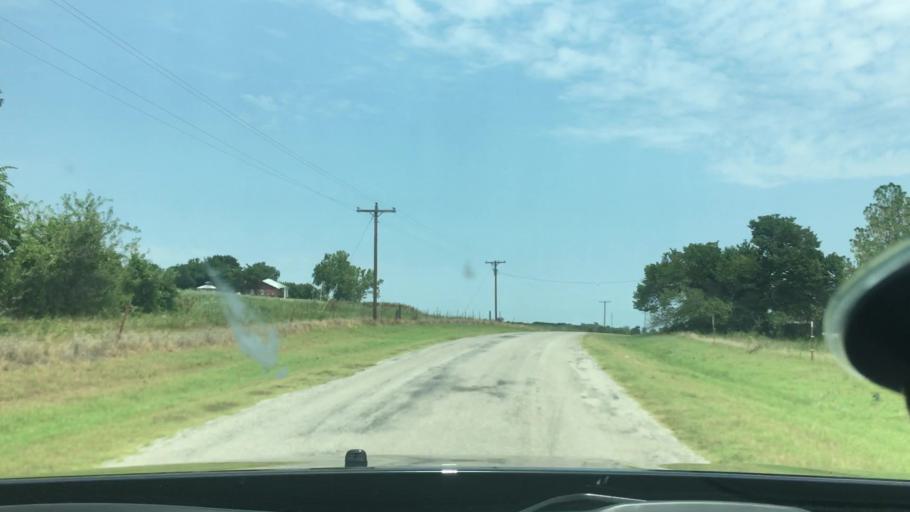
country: US
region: Texas
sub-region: Cooke County
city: Muenster
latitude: 33.8833
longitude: -97.3564
